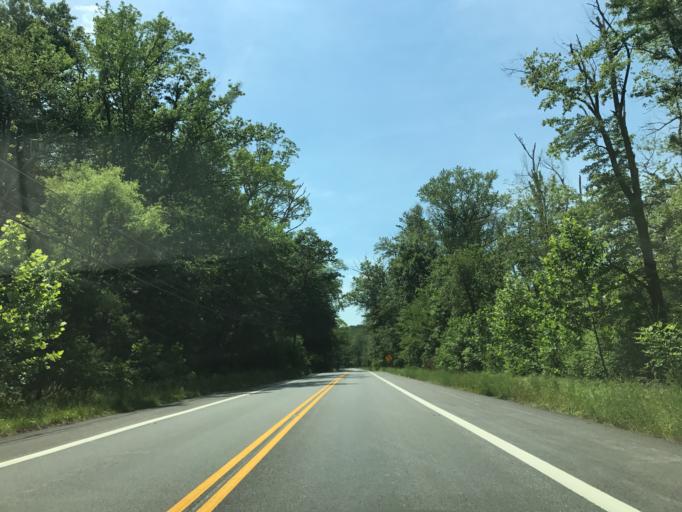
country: US
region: Maryland
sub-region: Anne Arundel County
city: Crownsville
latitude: 38.9912
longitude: -76.6312
